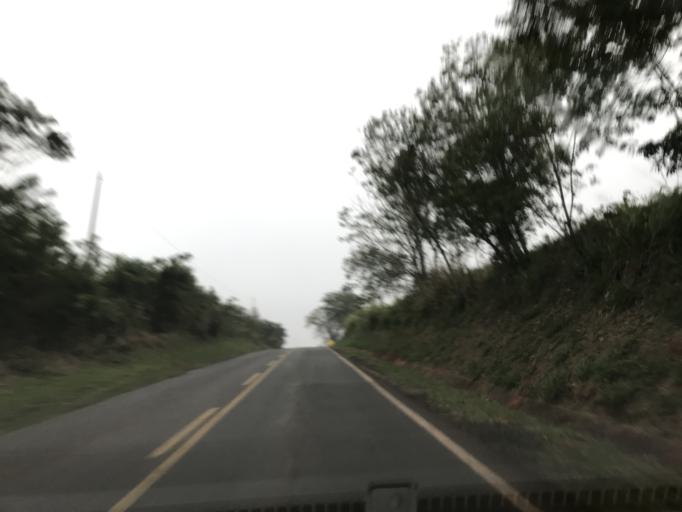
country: PY
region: Canindeyu
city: Salto del Guaira
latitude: -24.0902
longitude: -54.0936
